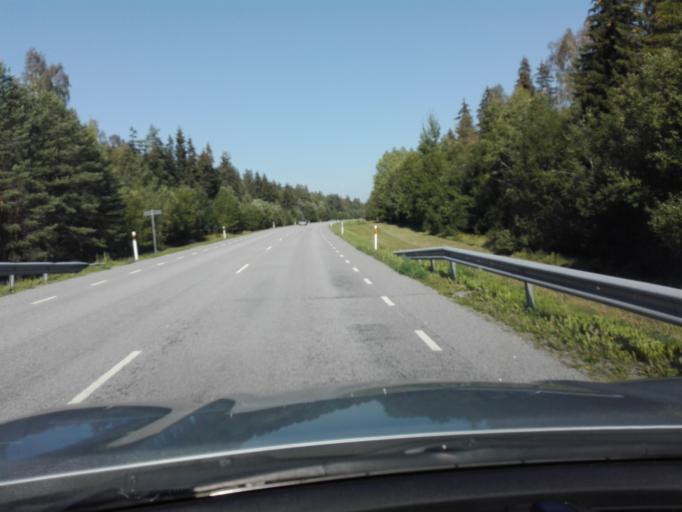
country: EE
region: Raplamaa
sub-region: Rapla vald
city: Rapla
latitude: 59.0061
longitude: 24.7692
